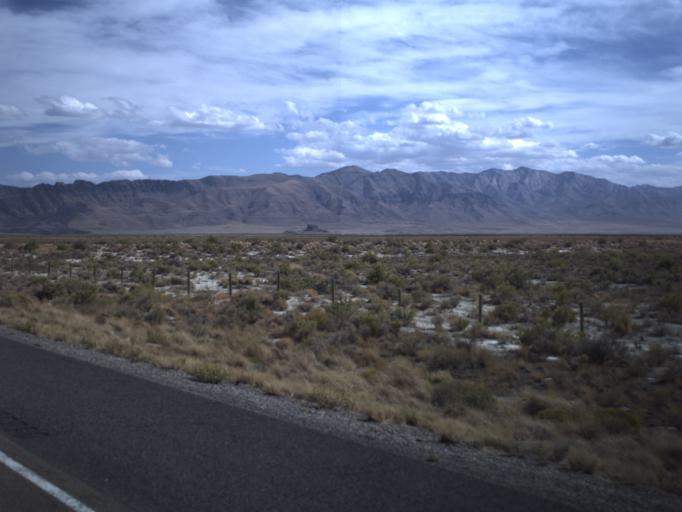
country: US
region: Utah
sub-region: Tooele County
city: Grantsville
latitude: 40.7552
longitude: -112.7484
